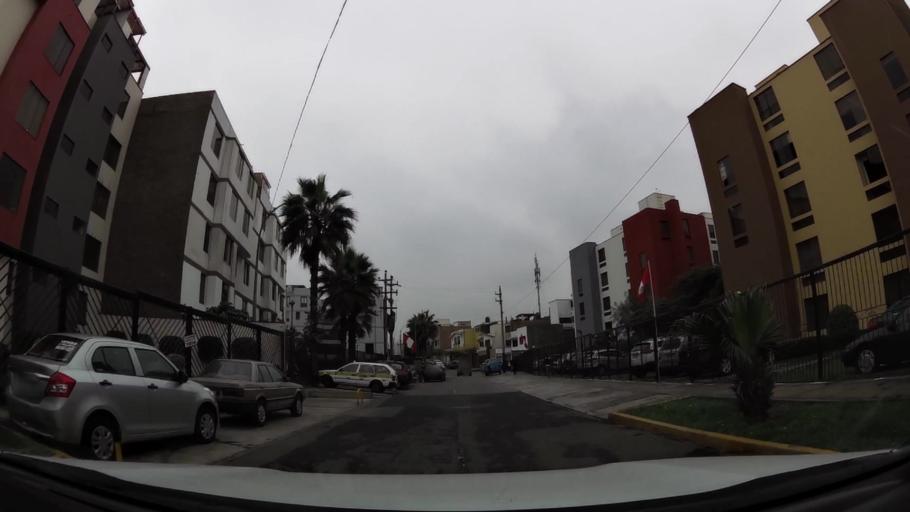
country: PE
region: Lima
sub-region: Lima
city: Surco
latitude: -12.1346
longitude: -77.0059
